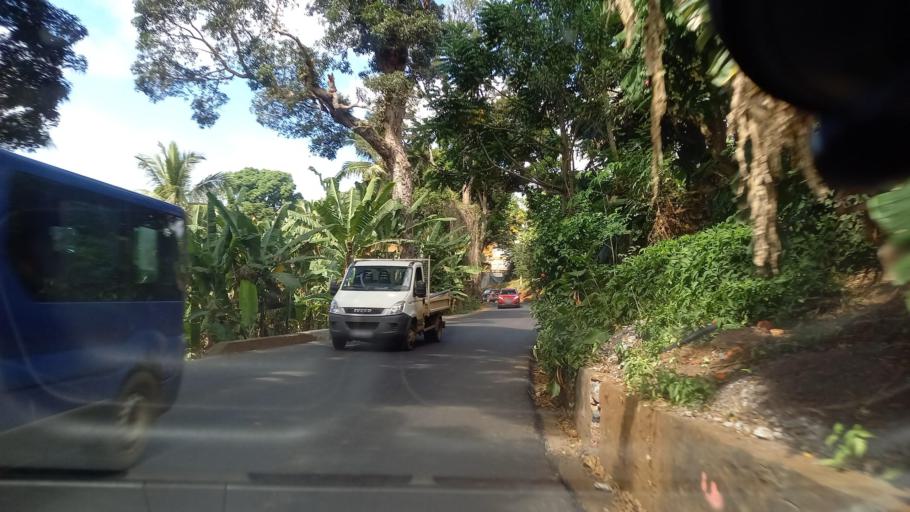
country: YT
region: Mamoudzou
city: Mamoudzou
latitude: -12.7899
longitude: 45.1794
